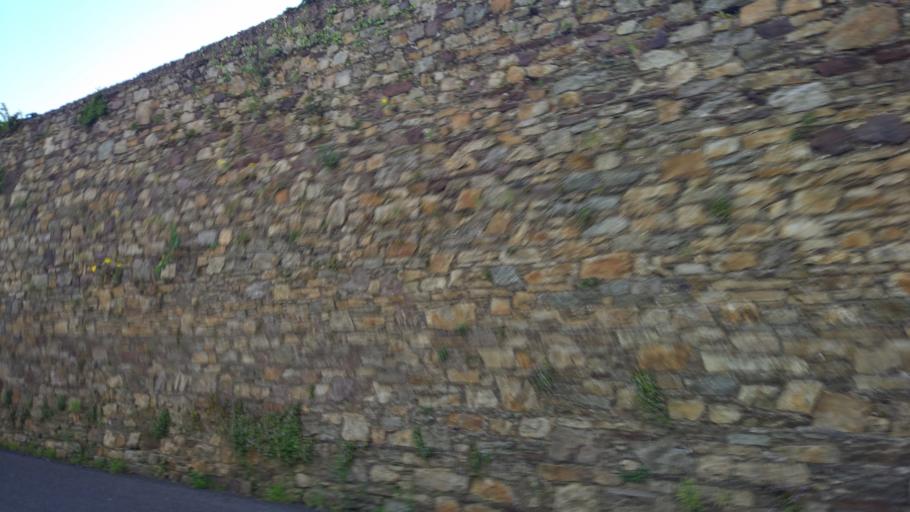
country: IE
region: Munster
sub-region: County Cork
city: Cork
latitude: 51.9090
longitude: -8.4607
